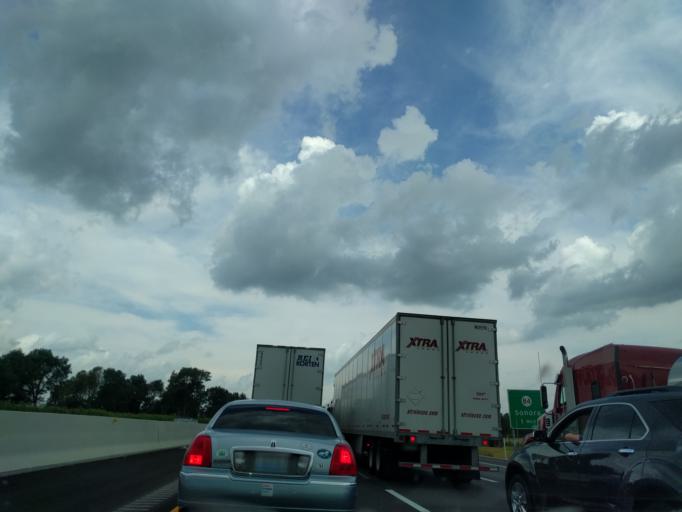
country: US
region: Kentucky
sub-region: Larue County
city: Hodgenville
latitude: 37.5021
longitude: -85.8874
